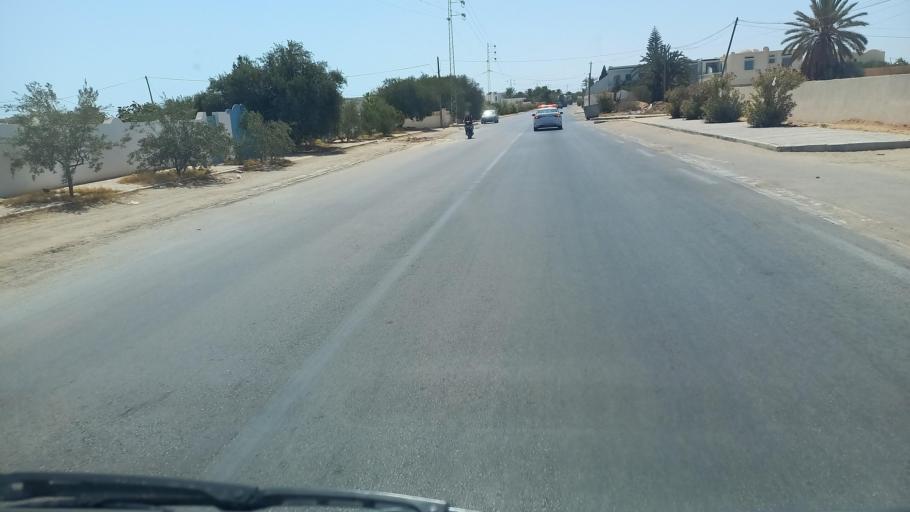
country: TN
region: Madanin
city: Houmt Souk
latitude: 33.7971
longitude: 10.8854
